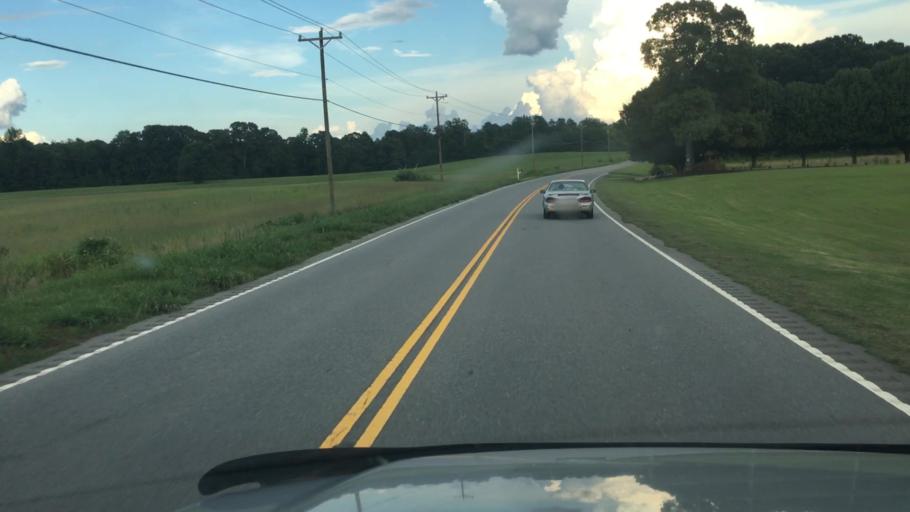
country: US
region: South Carolina
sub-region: Cherokee County
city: Gaffney
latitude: 35.1182
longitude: -81.7140
